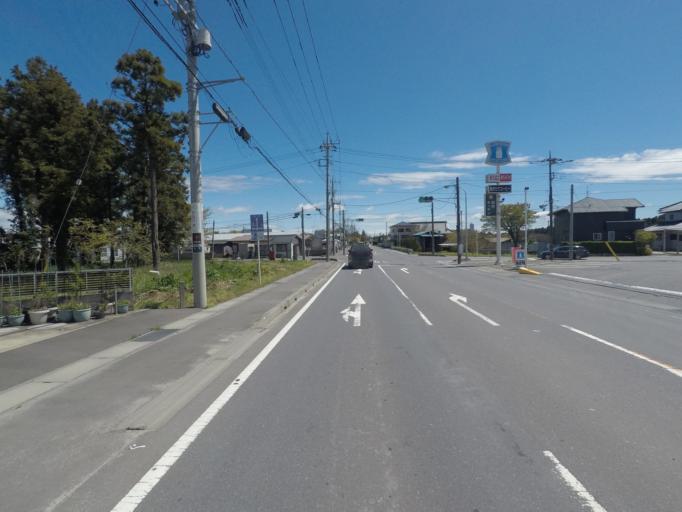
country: JP
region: Ibaraki
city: Ishioka
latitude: 36.0945
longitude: 140.3437
